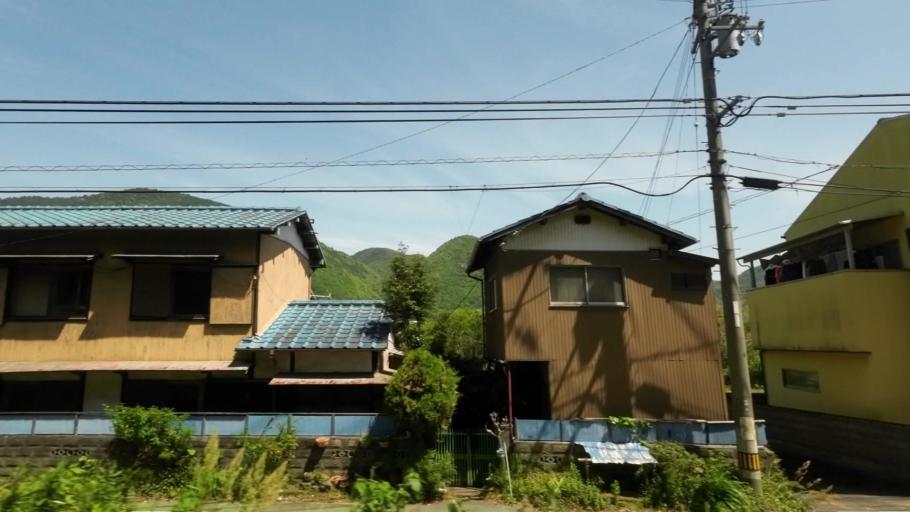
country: JP
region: Tokushima
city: Ikedacho
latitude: 34.0327
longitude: 133.8554
